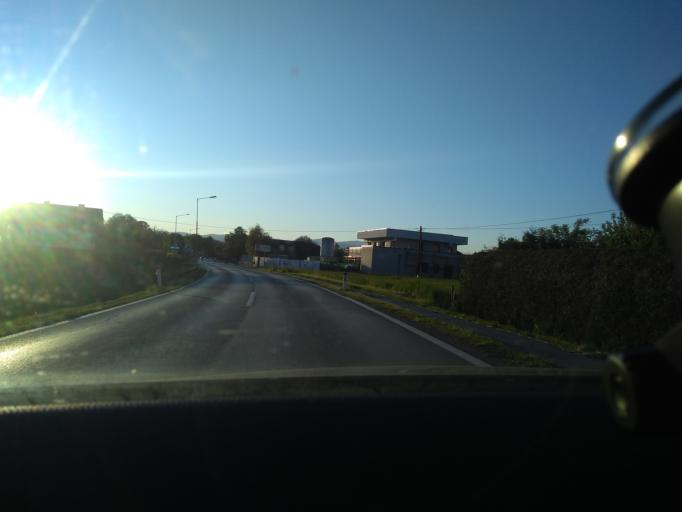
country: AT
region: Styria
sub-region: Politischer Bezirk Voitsberg
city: Mooskirchen
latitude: 46.9968
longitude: 15.2959
